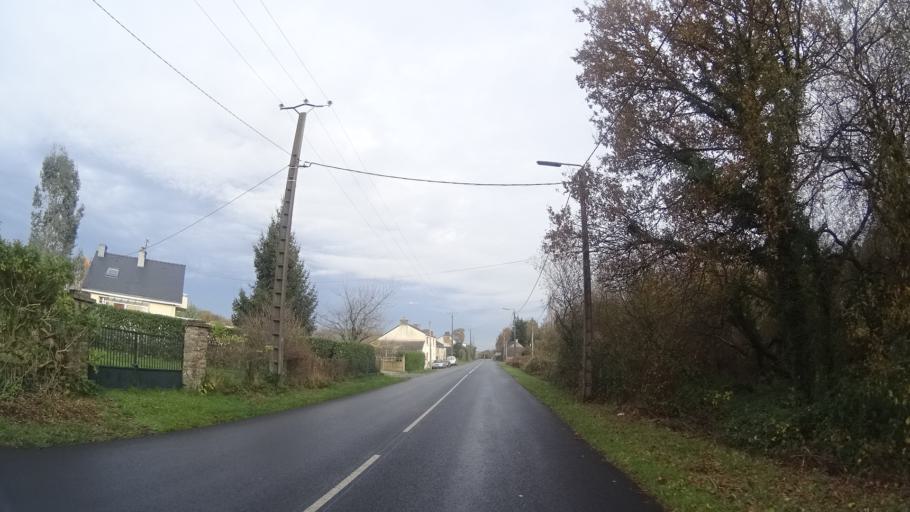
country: FR
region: Brittany
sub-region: Departement du Morbihan
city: Saint-Jean-la-Poterie
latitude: 47.6248
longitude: -2.1065
